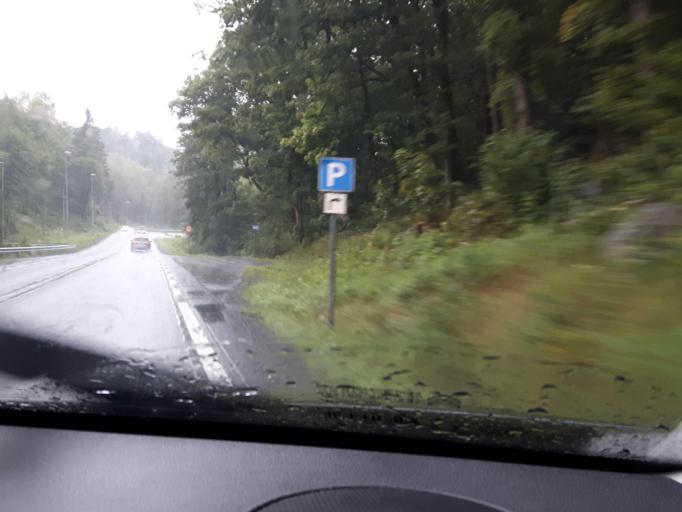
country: NO
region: Vest-Agder
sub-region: Lindesnes
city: Vigeland
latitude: 58.0536
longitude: 7.3765
